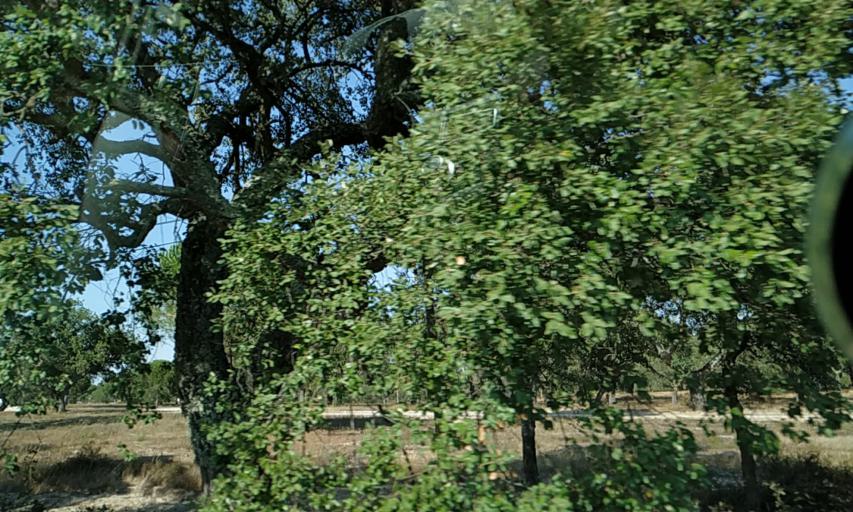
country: PT
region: Evora
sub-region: Vendas Novas
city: Vendas Novas
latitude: 38.7436
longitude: -8.6290
